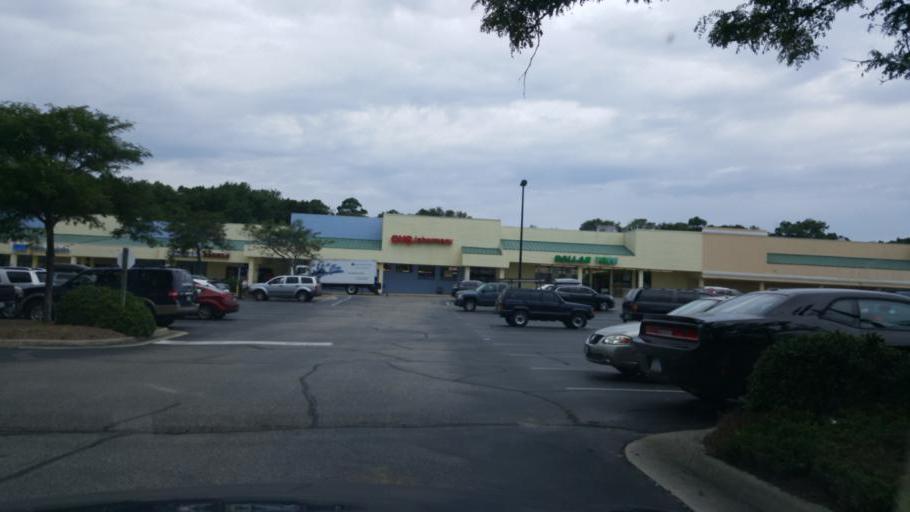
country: US
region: North Carolina
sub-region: Dare County
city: Kitty Hawk
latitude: 36.0991
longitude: -75.7233
